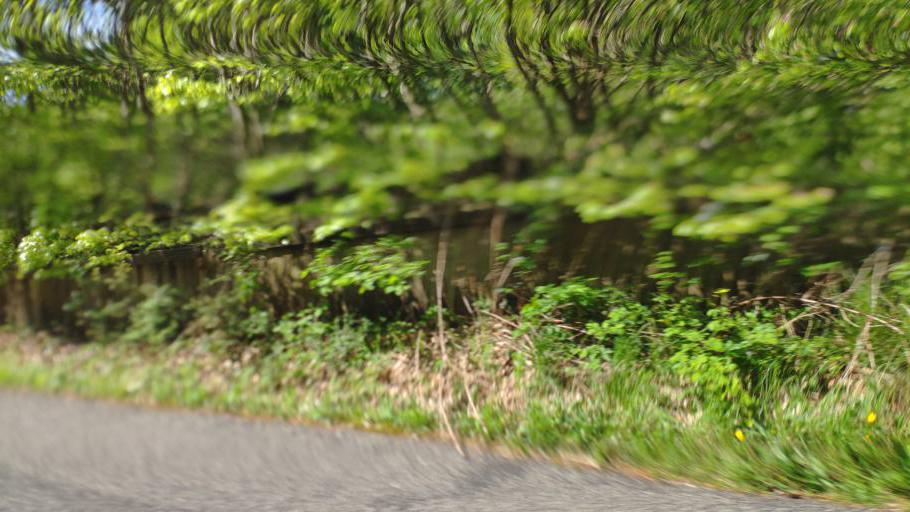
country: IE
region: Munster
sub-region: County Cork
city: Blarney
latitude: 51.9775
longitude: -8.5839
